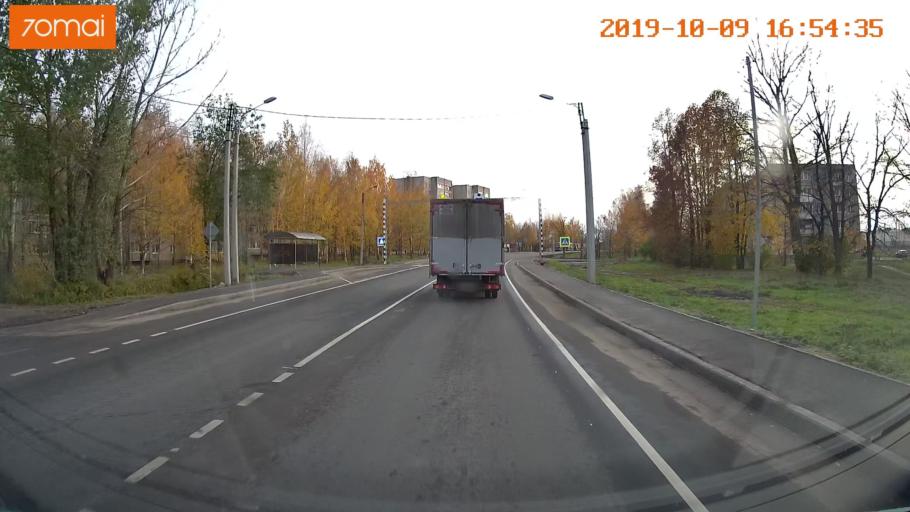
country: RU
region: Ivanovo
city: Privolzhsk
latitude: 57.3728
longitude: 41.2788
